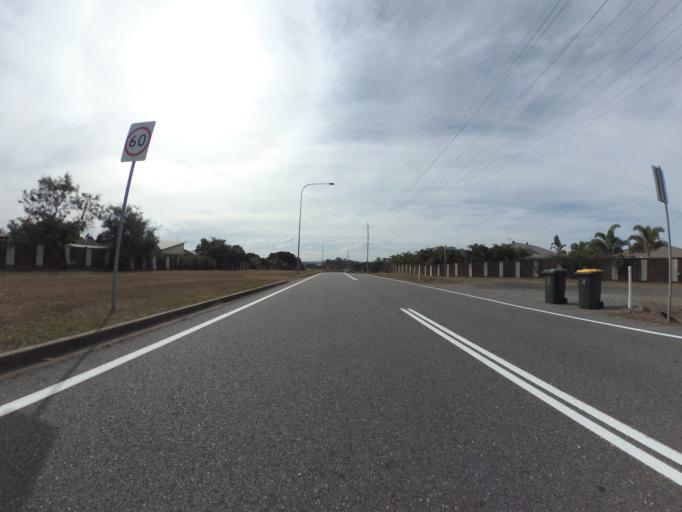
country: AU
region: Queensland
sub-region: Brisbane
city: Moggill
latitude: -27.5733
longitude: 152.8719
